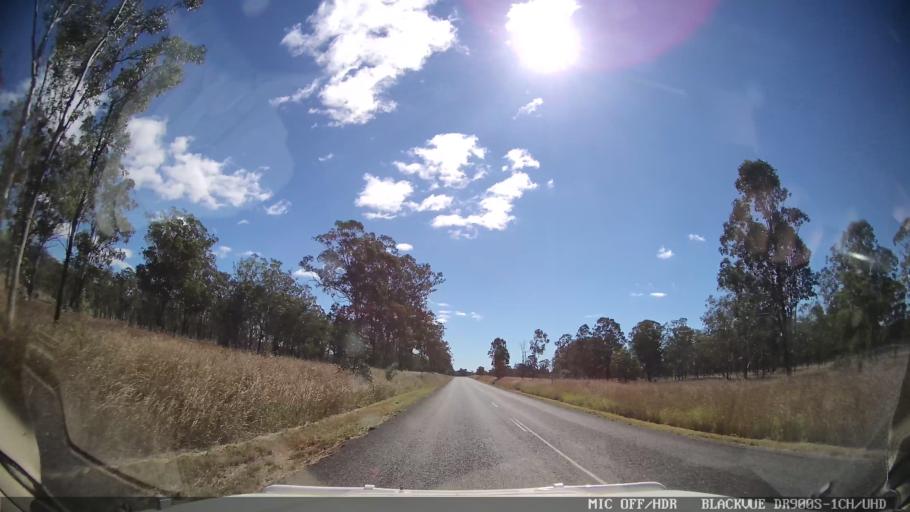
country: AU
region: Queensland
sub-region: Gladstone
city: Toolooa
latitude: -24.4428
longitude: 151.3413
